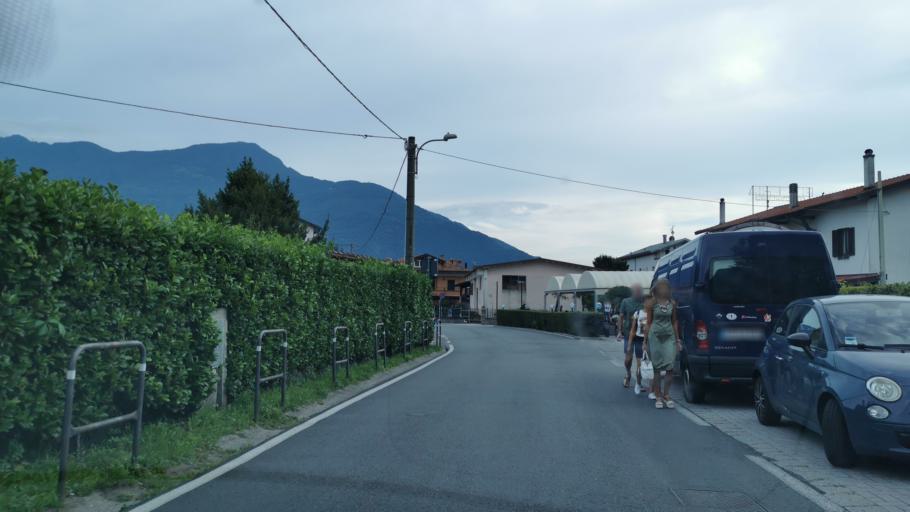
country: IT
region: Lombardy
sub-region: Provincia di Como
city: Domaso
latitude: 46.1523
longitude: 9.3318
